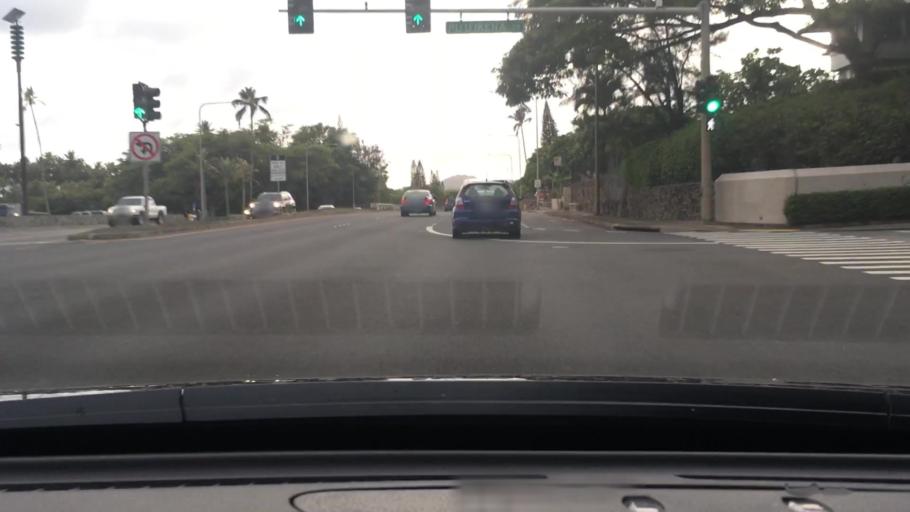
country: US
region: Hawaii
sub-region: Honolulu County
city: Waimanalo
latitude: 21.2801
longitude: -157.7444
